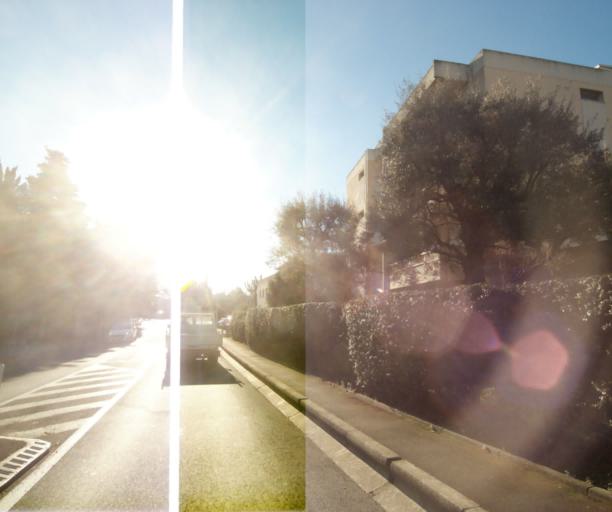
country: FR
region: Provence-Alpes-Cote d'Azur
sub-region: Departement des Alpes-Maritimes
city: Antibes
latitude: 43.5810
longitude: 7.1099
